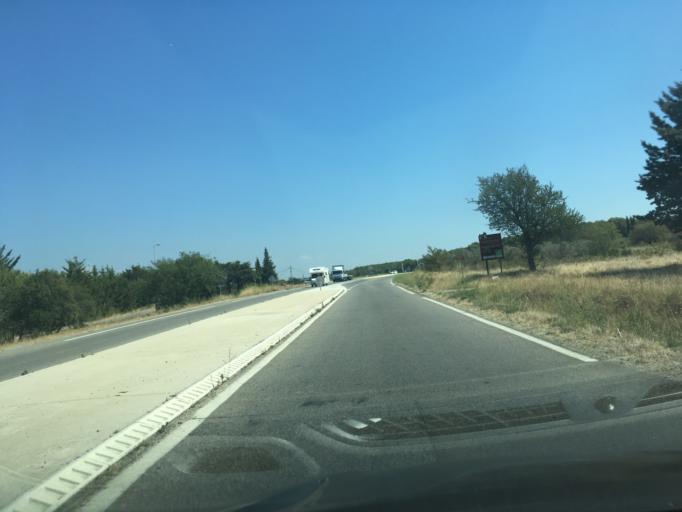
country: FR
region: Provence-Alpes-Cote d'Azur
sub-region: Departement des Bouches-du-Rhone
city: Lancon-Provence
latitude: 43.5848
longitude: 5.1379
